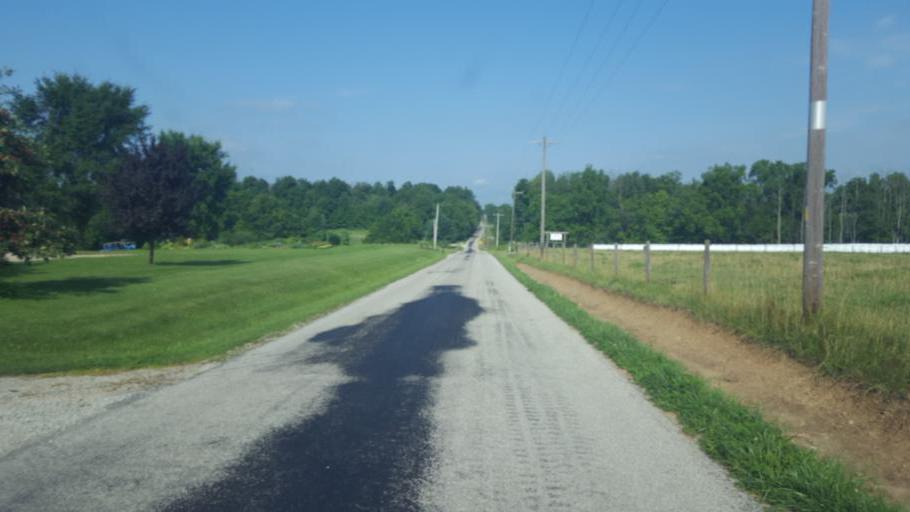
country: US
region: Ohio
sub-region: Morrow County
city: Mount Gilead
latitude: 40.6245
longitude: -82.7590
